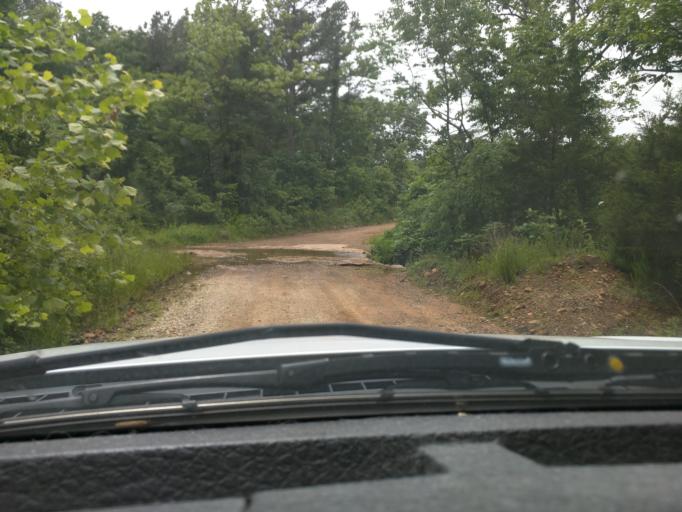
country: US
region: Arkansas
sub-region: Madison County
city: Huntsville
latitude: 35.8660
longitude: -93.5305
